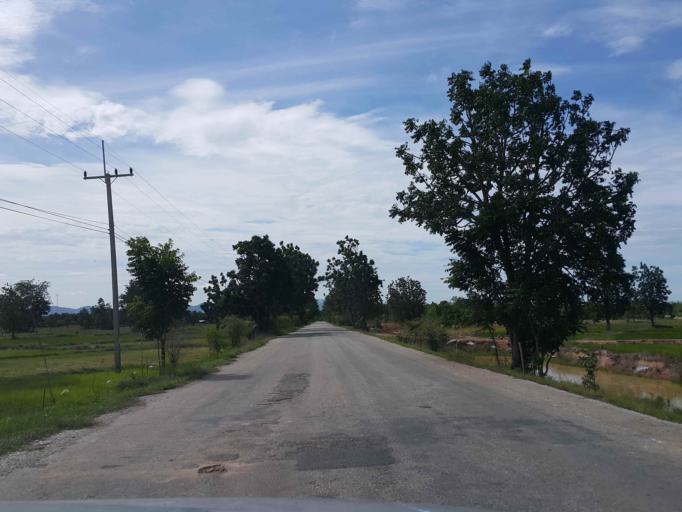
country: TH
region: Sukhothai
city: Ban Dan Lan Hoi
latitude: 17.1294
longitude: 99.5287
